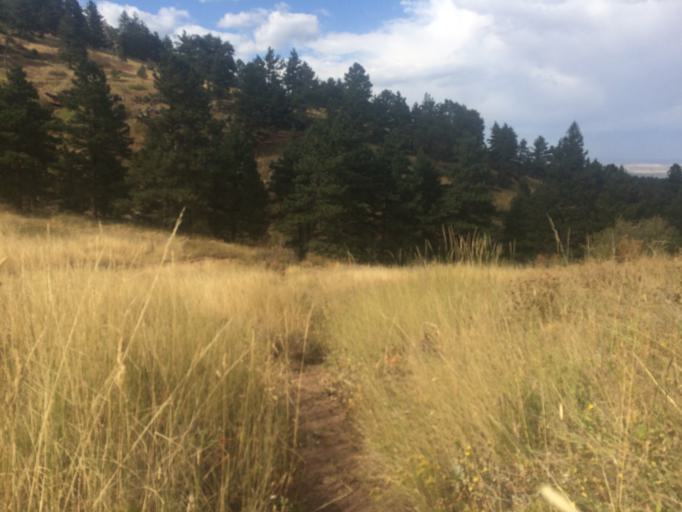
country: US
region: Colorado
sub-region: Boulder County
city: Boulder
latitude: 39.9786
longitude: -105.2836
